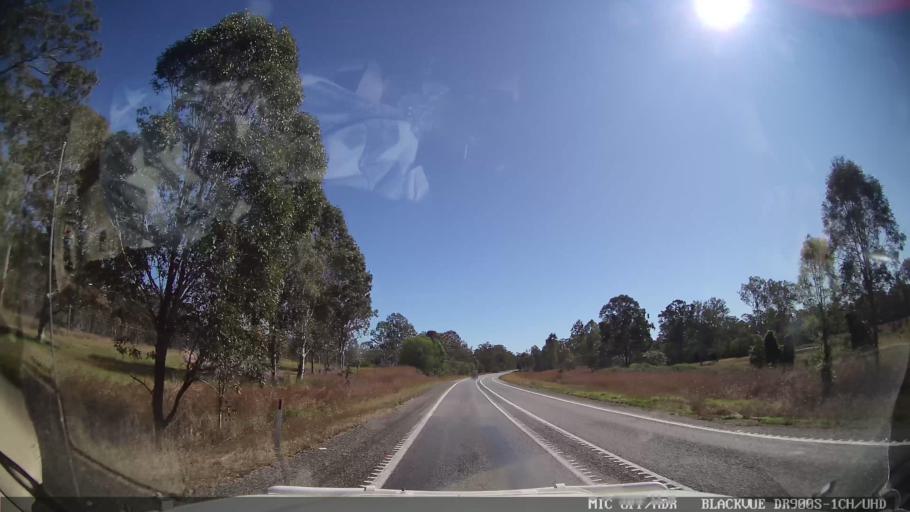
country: AU
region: Queensland
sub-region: Gympie Regional Council
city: Gympie
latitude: -26.0453
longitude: 152.5732
